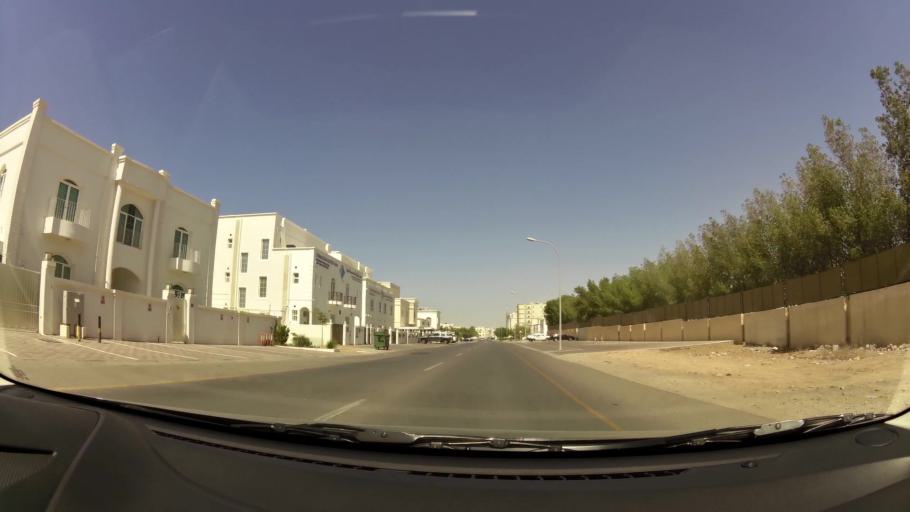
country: OM
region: Muhafazat Masqat
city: Bawshar
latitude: 23.5971
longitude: 58.3560
